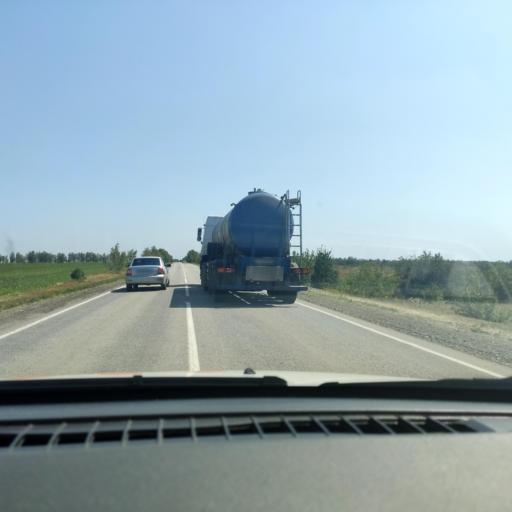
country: RU
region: Voronezj
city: Ostrogozhsk
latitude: 50.8025
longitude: 39.3188
